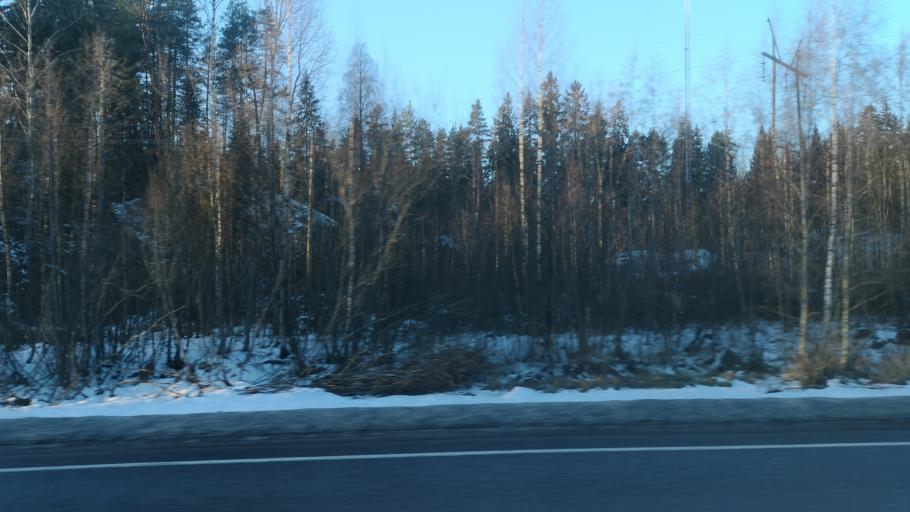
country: FI
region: Southern Savonia
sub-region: Pieksaemaeki
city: Juva
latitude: 61.7634
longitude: 27.5785
